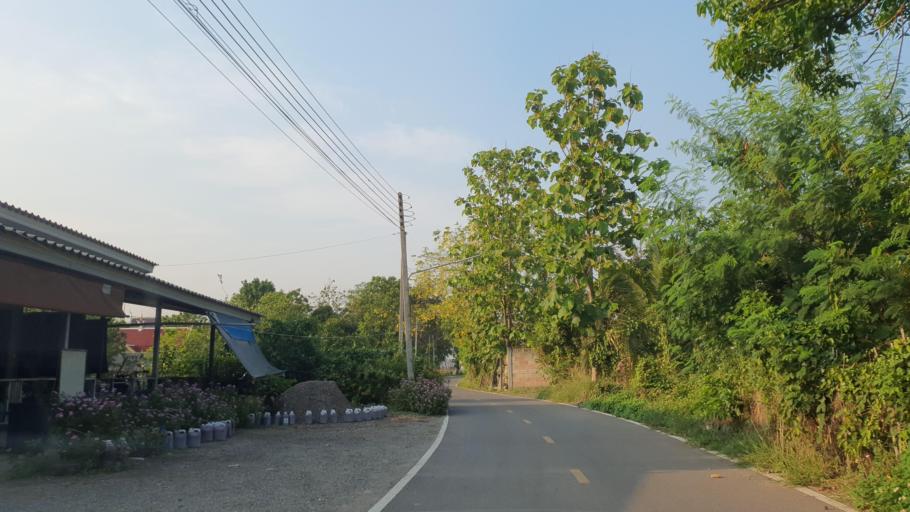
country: TH
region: Chiang Mai
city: San Pa Tong
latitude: 18.6437
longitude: 98.9101
